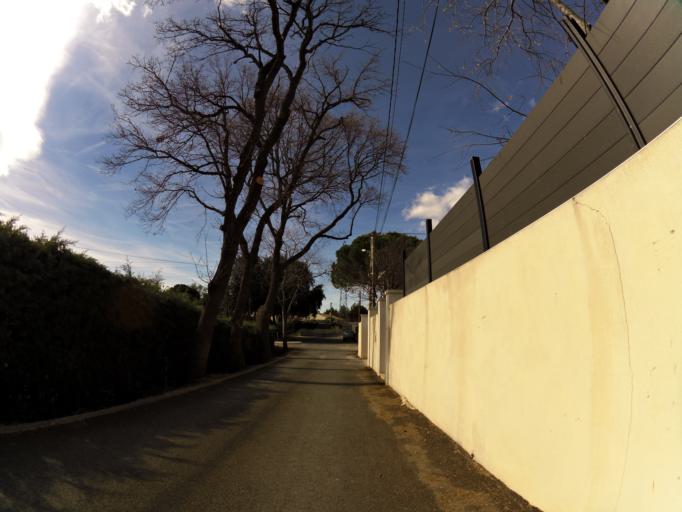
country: FR
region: Languedoc-Roussillon
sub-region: Departement du Gard
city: Mus
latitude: 43.7416
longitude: 4.1993
